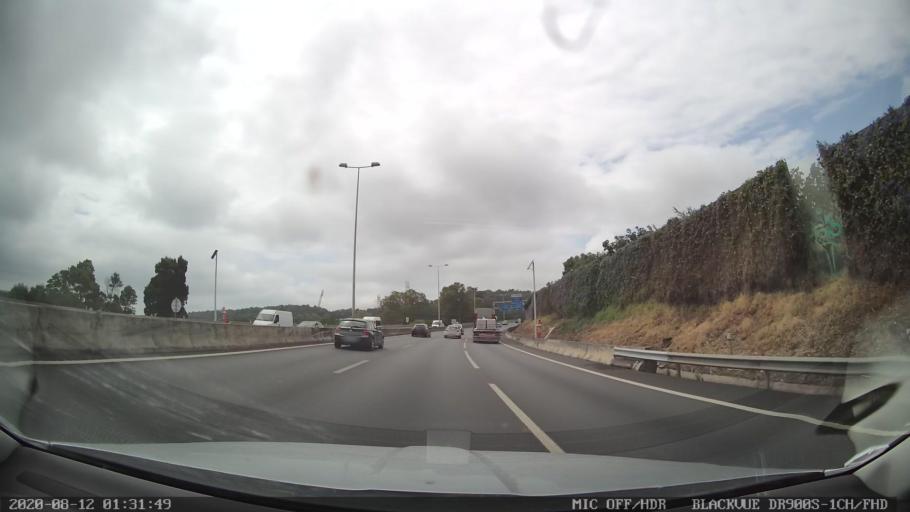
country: PT
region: Lisbon
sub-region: Oeiras
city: Linda-a-Velha
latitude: 38.7147
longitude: -9.2525
